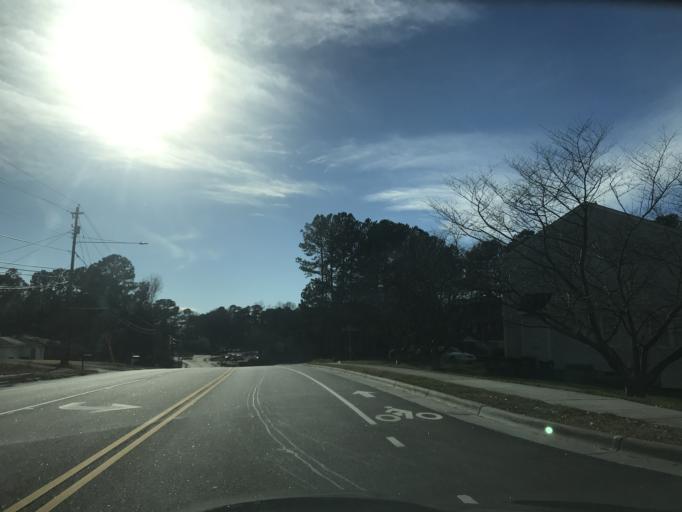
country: US
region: North Carolina
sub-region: Wake County
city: Cary
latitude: 35.7798
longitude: -78.7299
